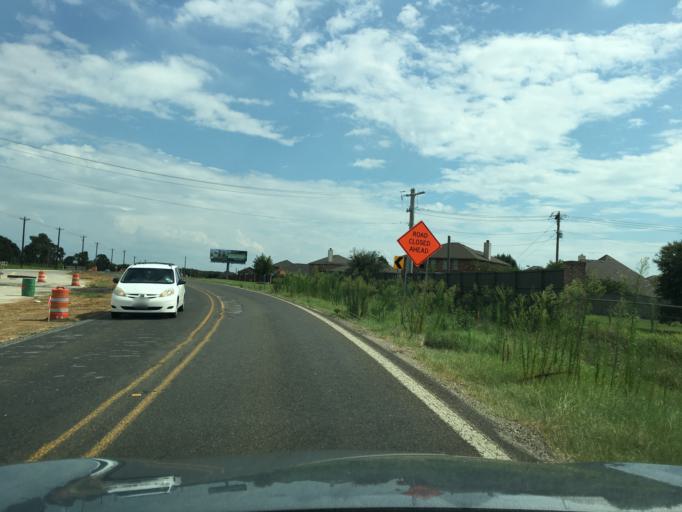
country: US
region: Texas
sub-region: Denton County
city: Cross Roads
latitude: 33.2160
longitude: -96.9767
